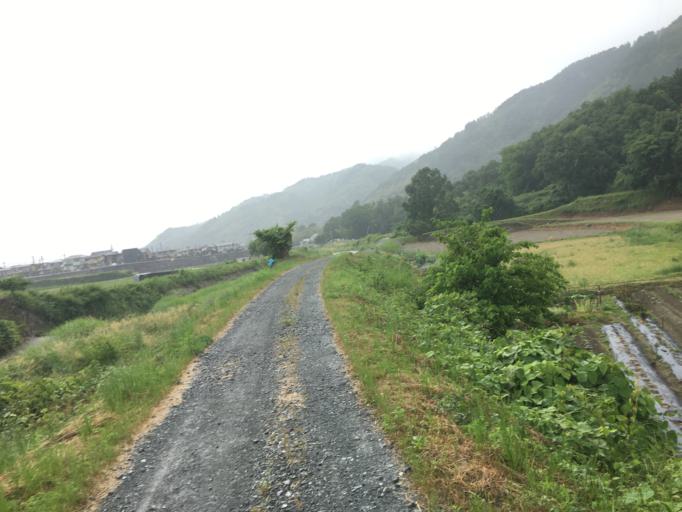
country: JP
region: Kyoto
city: Kameoka
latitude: 35.0062
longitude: 135.6129
